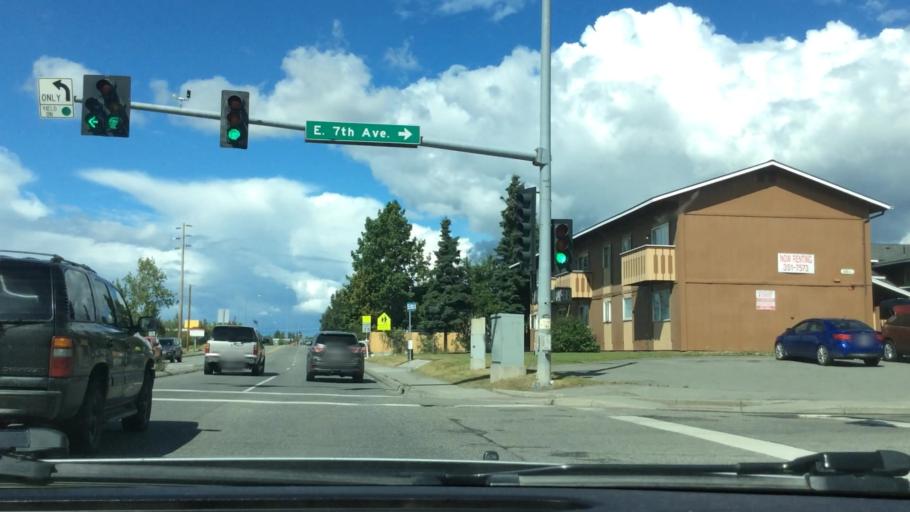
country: US
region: Alaska
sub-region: Anchorage Municipality
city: Anchorage
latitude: 61.2158
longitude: -149.8082
